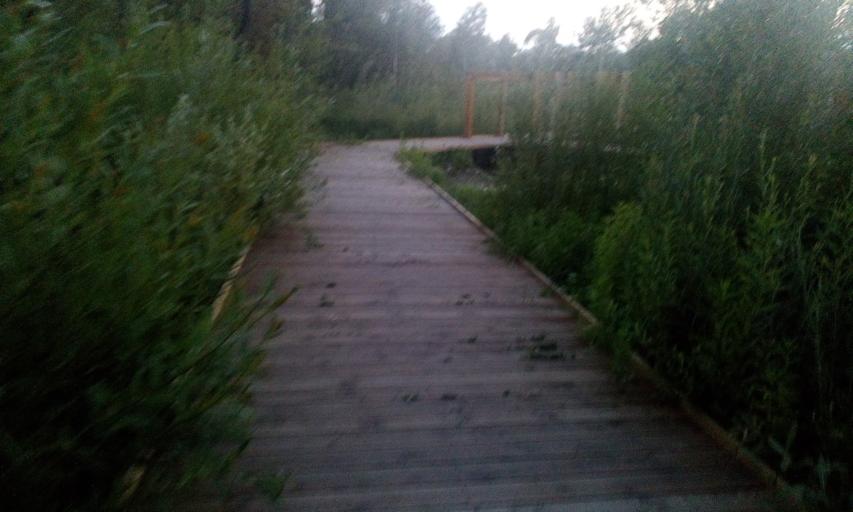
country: PL
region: Lesser Poland Voivodeship
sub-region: Powiat nowosadecki
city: Stary Sacz
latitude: 49.5846
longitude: 20.6445
